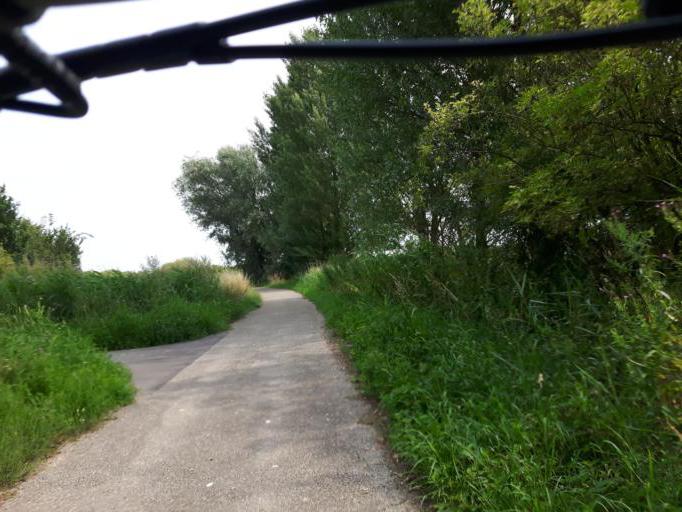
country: NL
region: Zeeland
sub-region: Gemeente Reimerswaal
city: Yerseke
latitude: 51.4833
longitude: 3.9738
